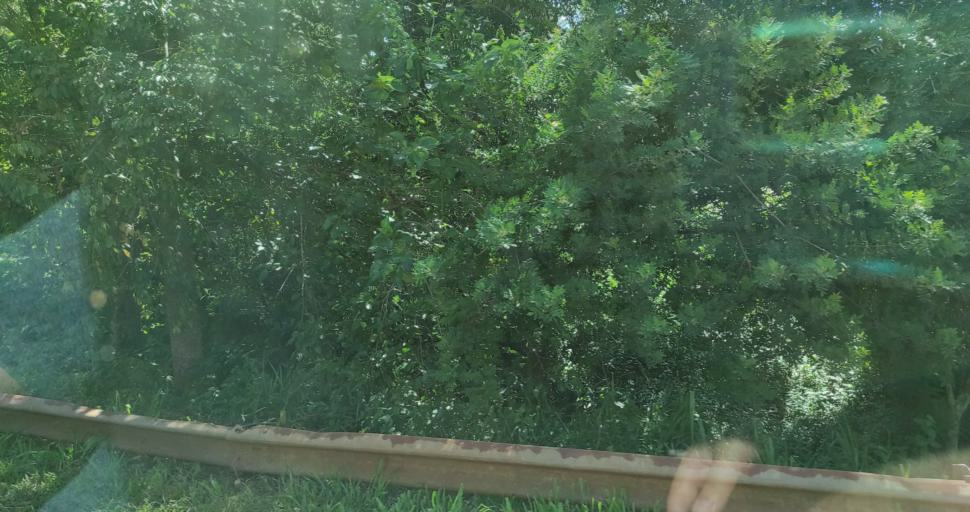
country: AR
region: Misiones
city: El Soberbio
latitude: -27.2826
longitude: -54.1967
